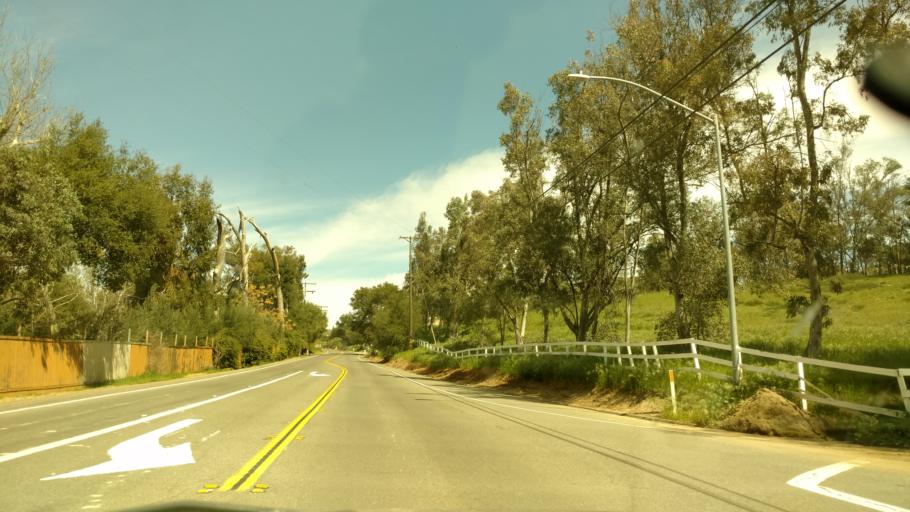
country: US
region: California
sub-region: San Diego County
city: San Diego Country Estates
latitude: 33.0783
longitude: -116.7978
